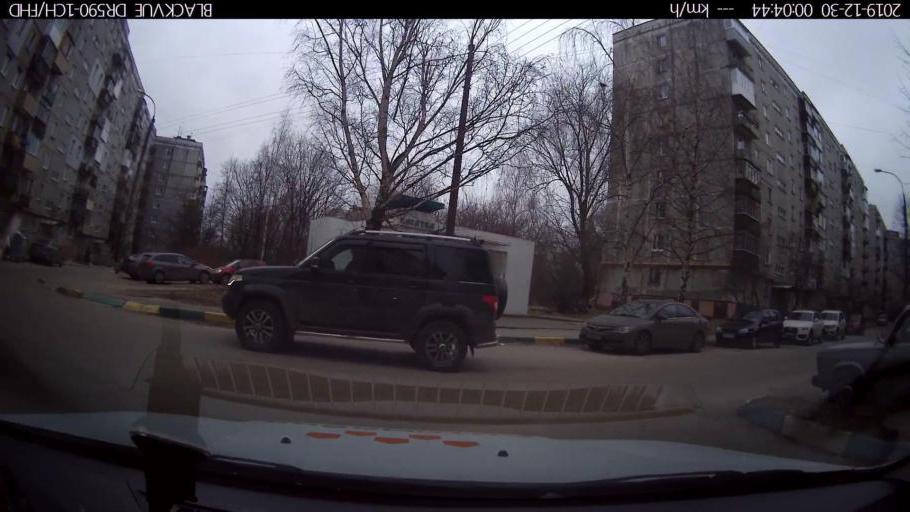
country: RU
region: Nizjnij Novgorod
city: Nizhniy Novgorod
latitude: 56.3126
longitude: 44.0487
